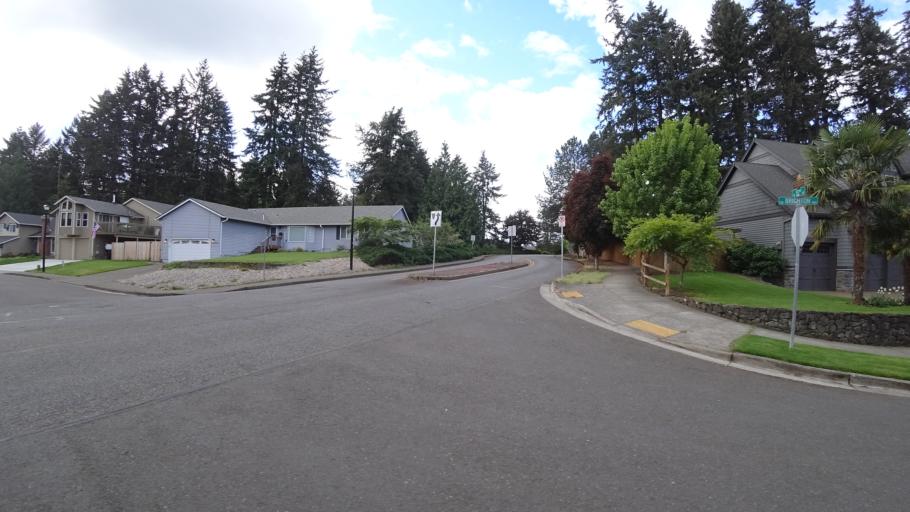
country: US
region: Oregon
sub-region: Washington County
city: Beaverton
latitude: 45.4697
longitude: -122.8339
